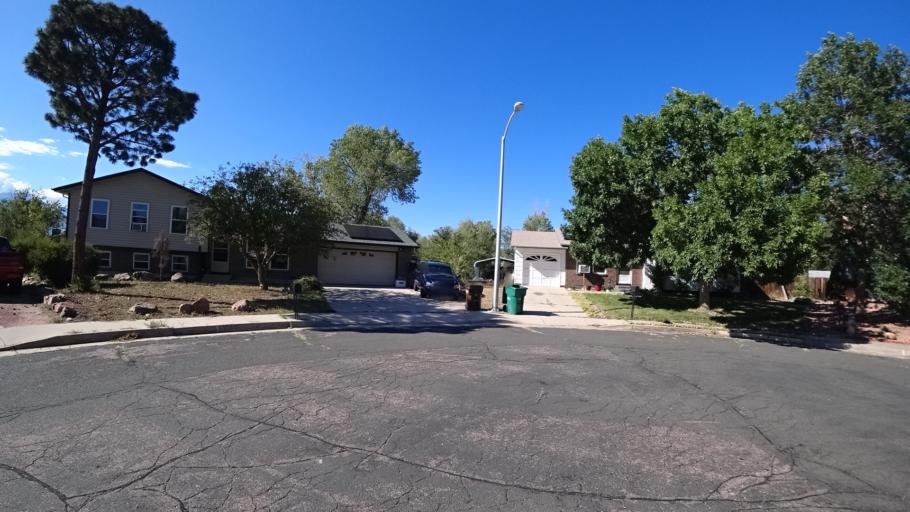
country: US
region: Colorado
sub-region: El Paso County
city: Stratmoor
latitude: 38.7974
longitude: -104.7543
